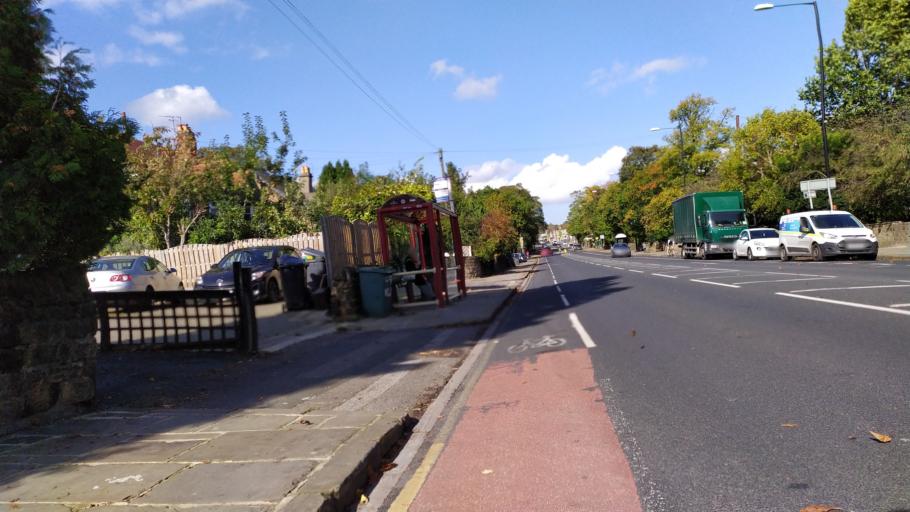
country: GB
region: England
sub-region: City and Borough of Leeds
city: Chapel Allerton
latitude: 53.8242
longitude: -1.5806
